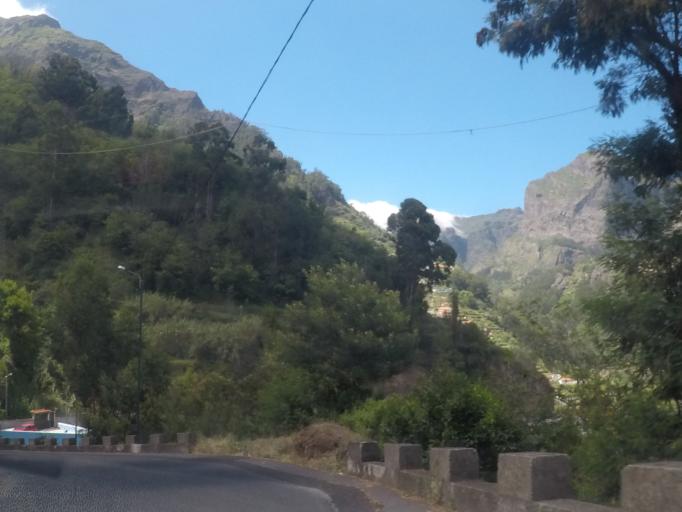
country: PT
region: Madeira
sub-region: Camara de Lobos
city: Curral das Freiras
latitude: 32.7105
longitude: -16.9732
